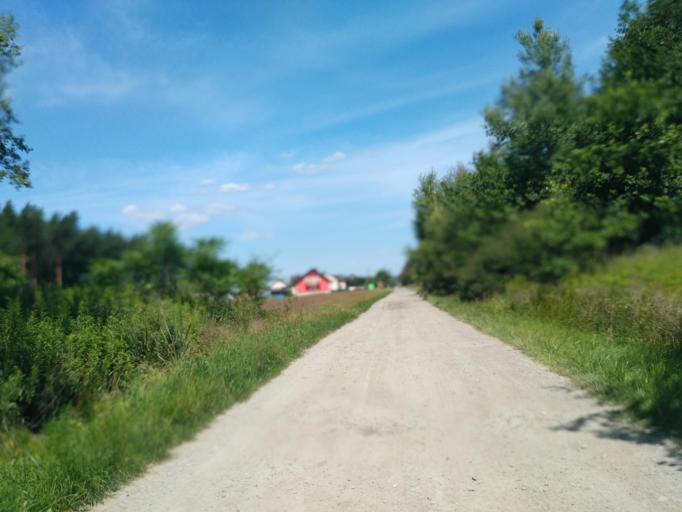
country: PL
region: Subcarpathian Voivodeship
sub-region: Powiat krosnienski
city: Kroscienko Wyzne
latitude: 49.6485
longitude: 21.8499
